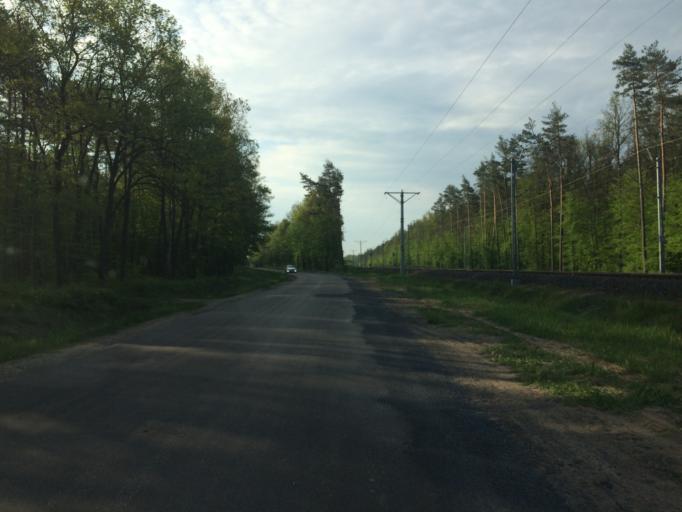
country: PL
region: Warmian-Masurian Voivodeship
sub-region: Powiat dzialdowski
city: Rybno
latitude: 53.3642
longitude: 19.9408
